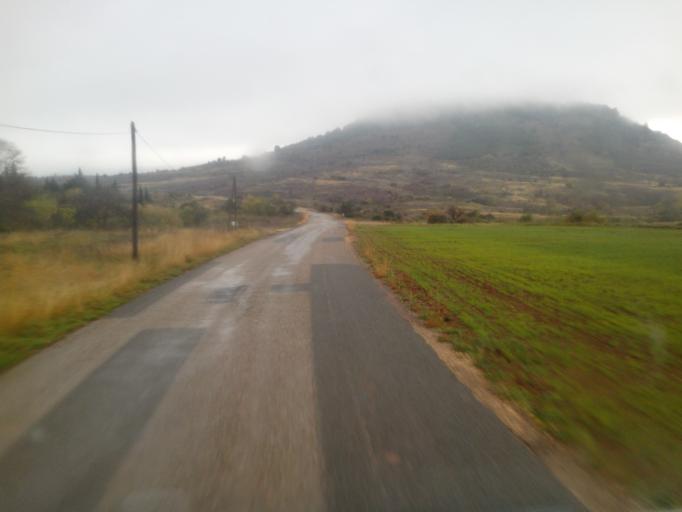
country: FR
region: Languedoc-Roussillon
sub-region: Departement de l'Herault
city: Lodeve
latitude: 43.6455
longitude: 3.3513
